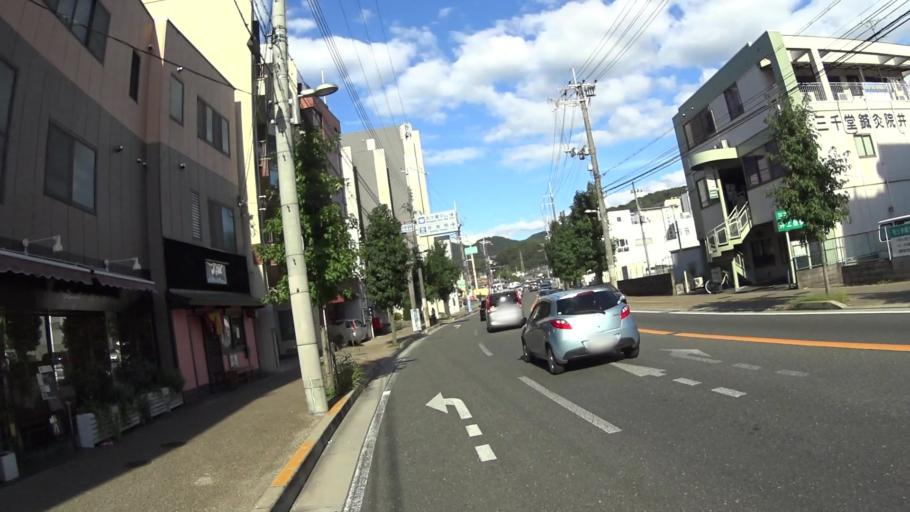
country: JP
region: Kyoto
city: Uji
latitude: 34.8901
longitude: 135.8038
